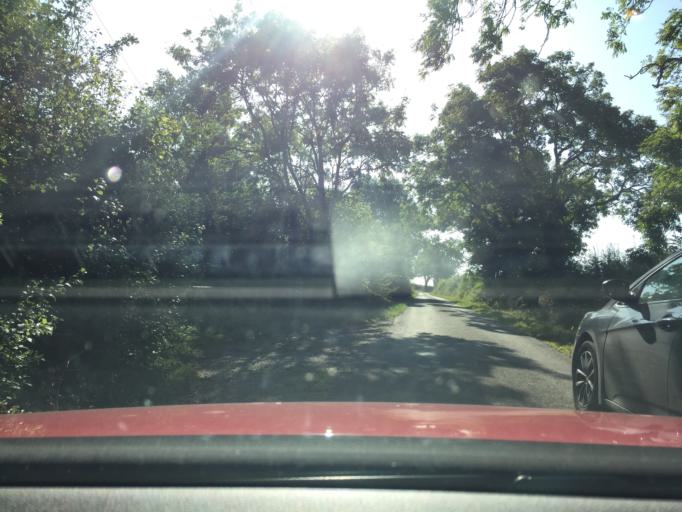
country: GB
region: England
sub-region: Leicestershire
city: Houghton on the Hill
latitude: 52.6381
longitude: -0.9308
